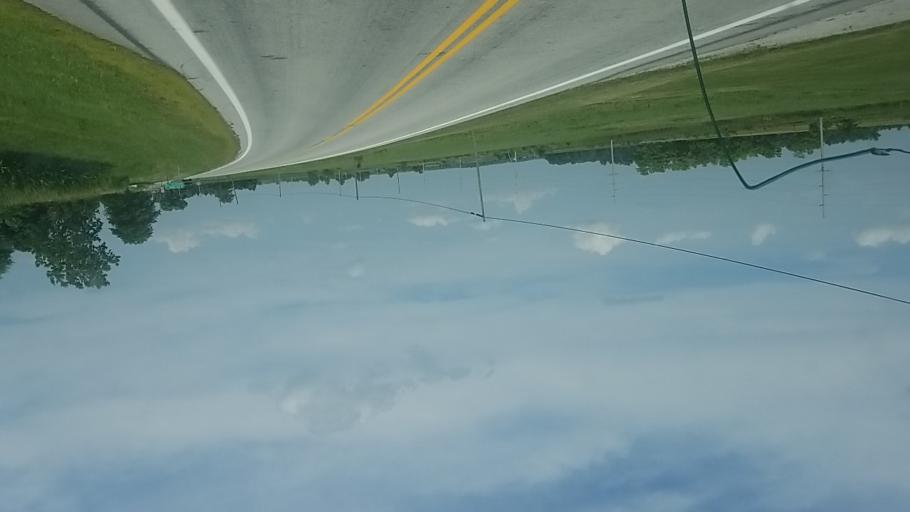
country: US
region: Ohio
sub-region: Hardin County
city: Forest
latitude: 40.8034
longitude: -83.4922
